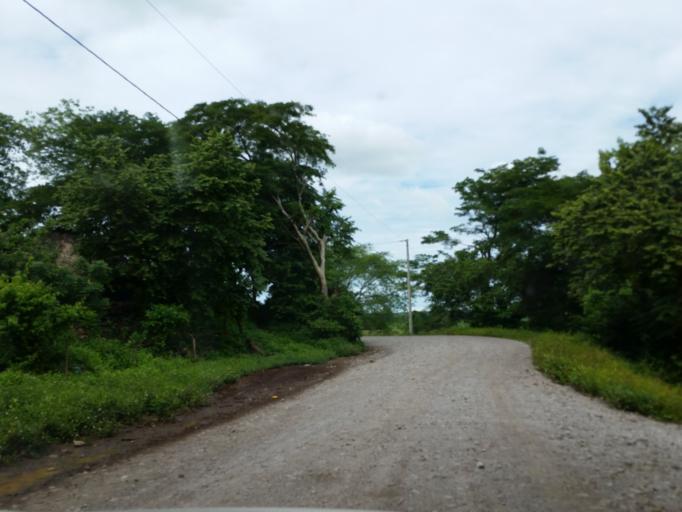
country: NI
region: Leon
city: Telica
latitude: 12.6952
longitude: -86.8585
